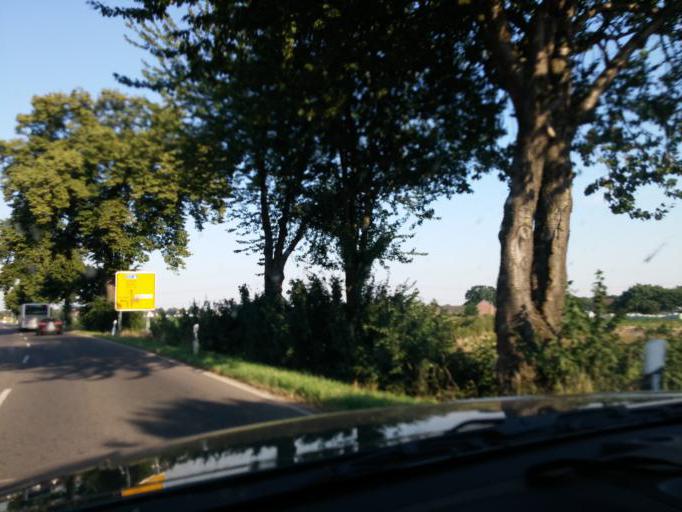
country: DE
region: North Rhine-Westphalia
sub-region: Regierungsbezirk Dusseldorf
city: Viersen
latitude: 51.2618
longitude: 6.4593
